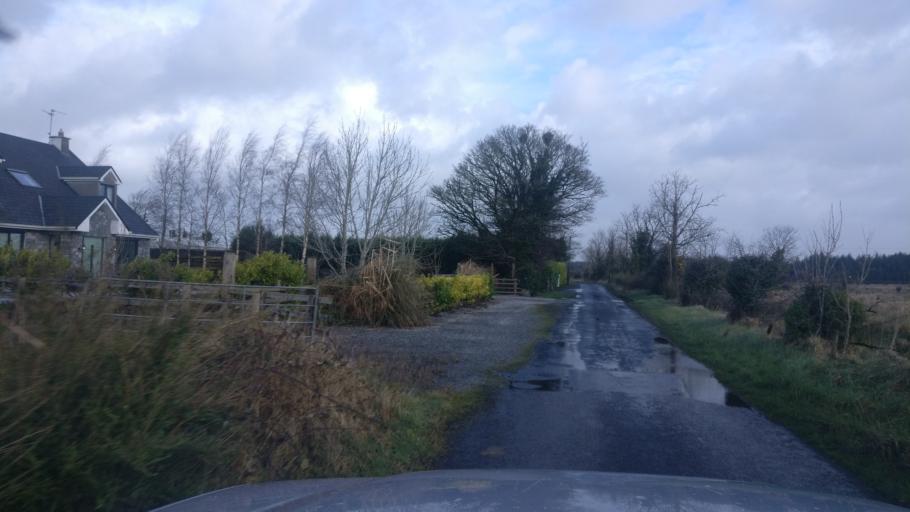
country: IE
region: Connaught
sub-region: County Galway
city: Loughrea
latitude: 53.2298
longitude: -8.5369
